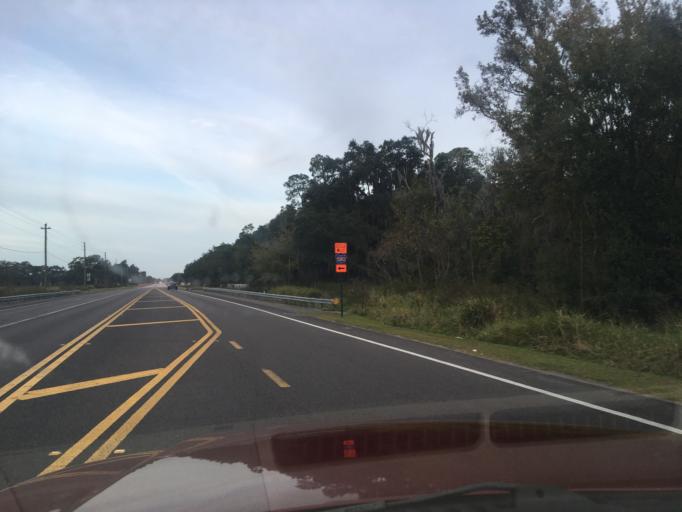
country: US
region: Florida
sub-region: Hillsborough County
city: Plant City
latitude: 28.0476
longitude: -82.1043
